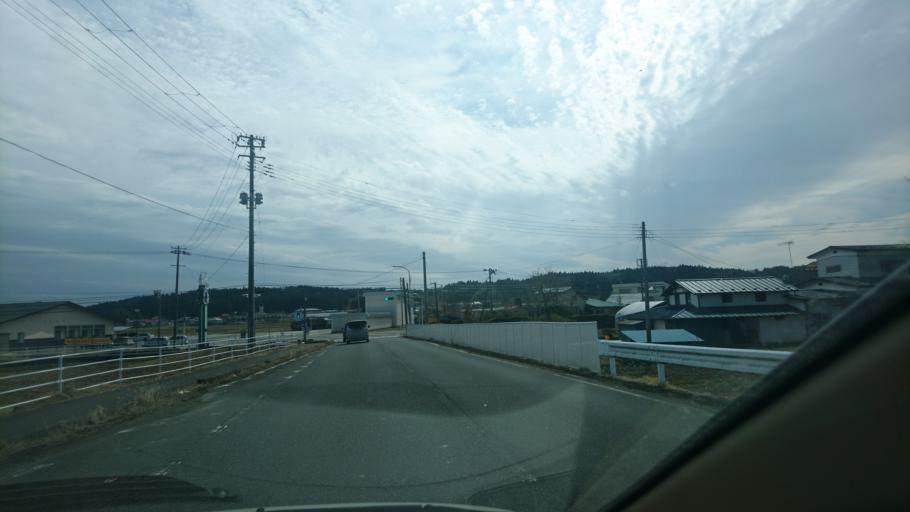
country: JP
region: Miyagi
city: Furukawa
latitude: 38.7406
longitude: 140.9466
